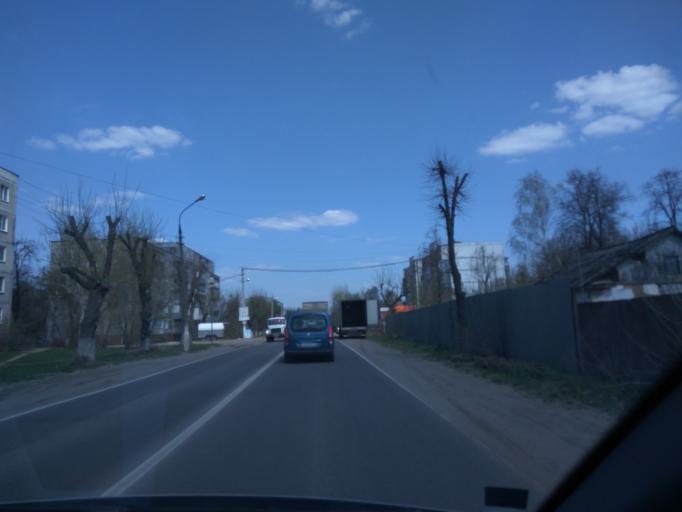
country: RU
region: Moskovskaya
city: Ramenskoye
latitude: 55.5498
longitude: 38.2530
